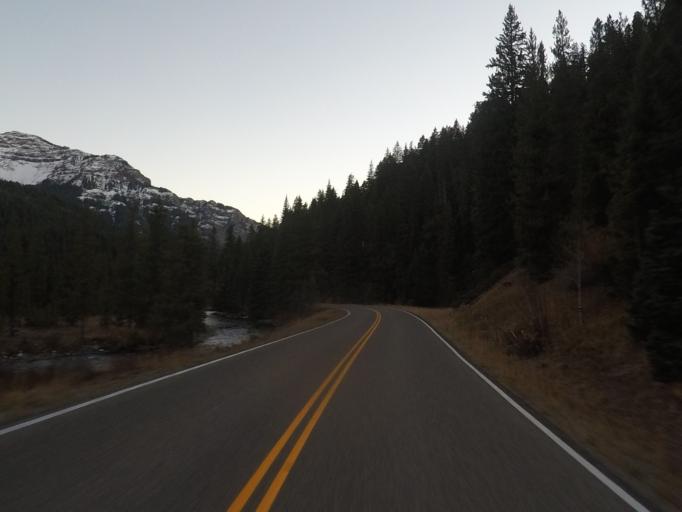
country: US
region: Montana
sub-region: Stillwater County
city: Absarokee
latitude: 44.9380
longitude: -110.0833
